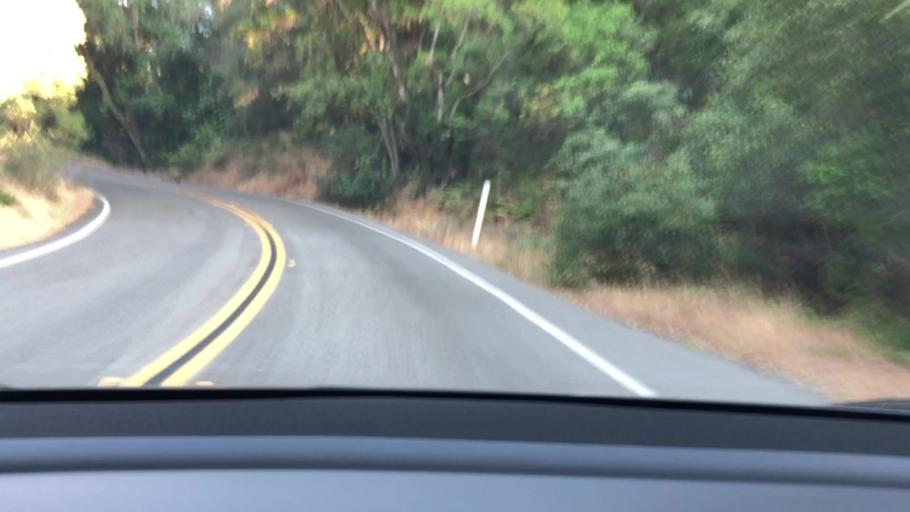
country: US
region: California
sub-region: Santa Clara County
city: Saratoga
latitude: 37.2775
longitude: -122.0718
